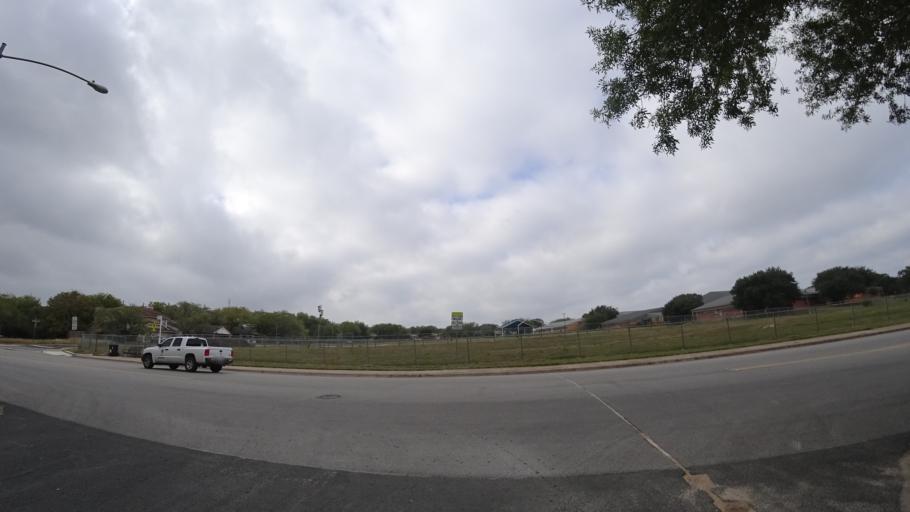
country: US
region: Texas
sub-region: Travis County
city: Shady Hollow
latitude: 30.2042
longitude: -97.8383
